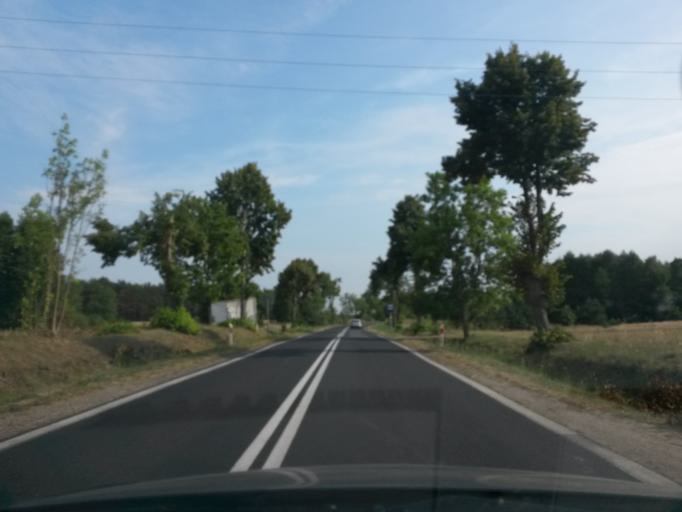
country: PL
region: Masovian Voivodeship
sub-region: Powiat sierpecki
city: Szczutowo
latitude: 52.9485
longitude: 19.5843
